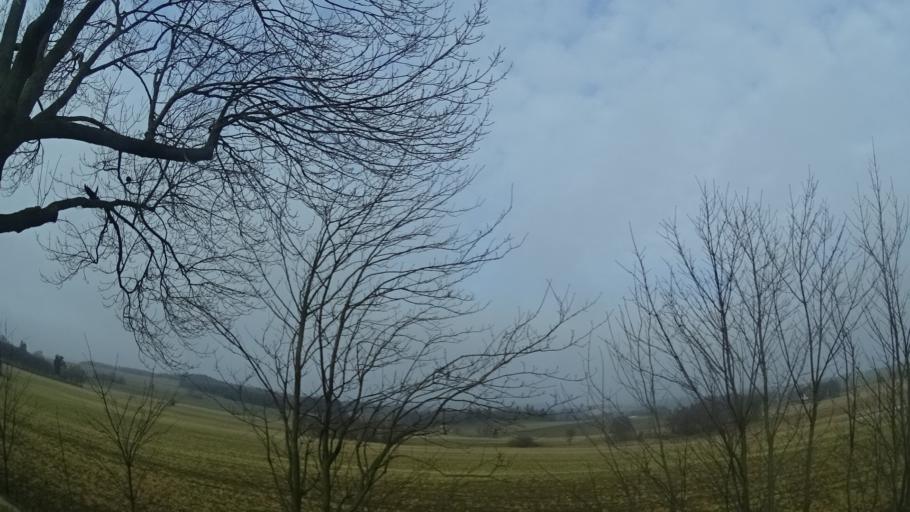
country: DE
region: Thuringia
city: Tanna
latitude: 50.4872
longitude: 11.8372
